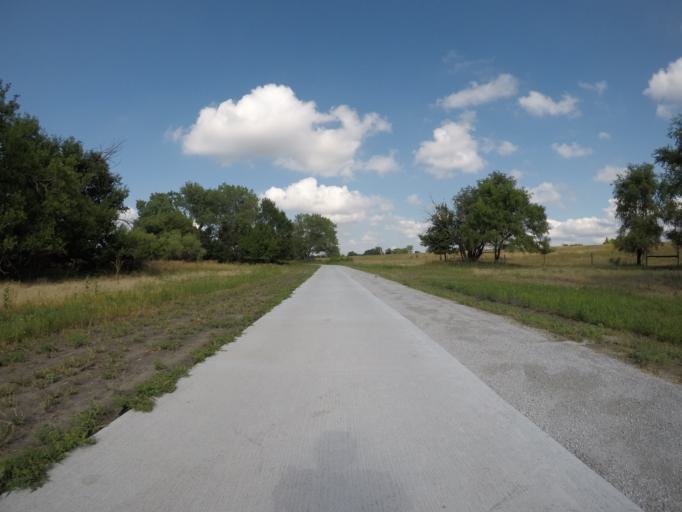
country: US
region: Nebraska
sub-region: Buffalo County
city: Kearney
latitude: 40.6766
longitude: -99.0023
